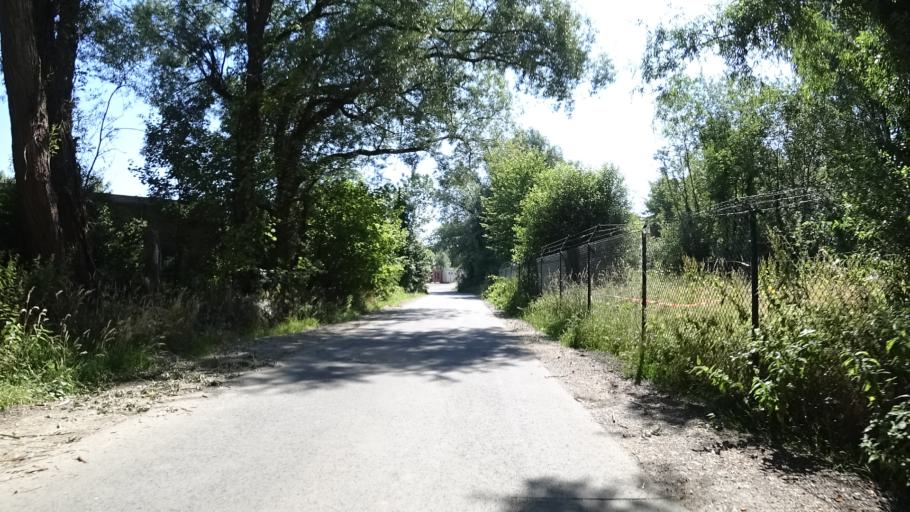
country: BE
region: Wallonia
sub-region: Province du Brabant Wallon
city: Incourt
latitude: 50.6967
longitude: 4.8211
